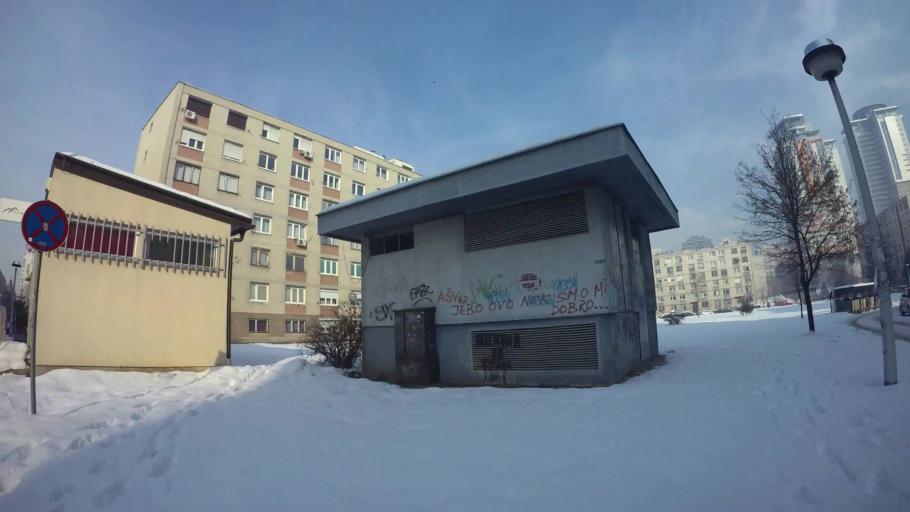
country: BA
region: Federation of Bosnia and Herzegovina
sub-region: Kanton Sarajevo
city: Sarajevo
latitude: 43.8469
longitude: 18.3703
